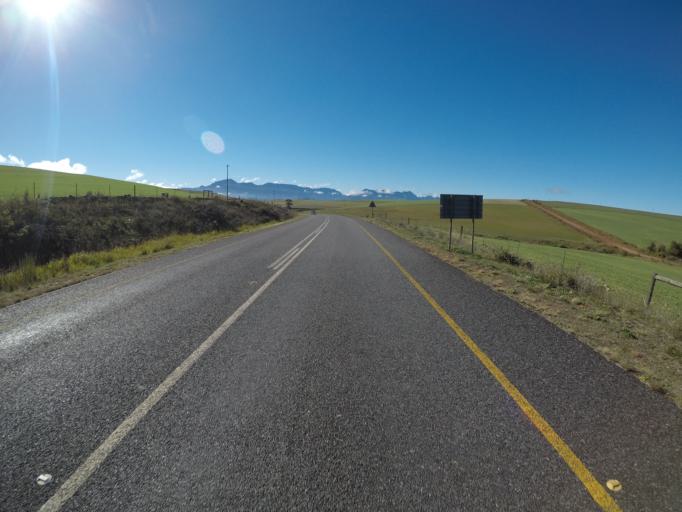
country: ZA
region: Western Cape
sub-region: Overberg District Municipality
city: Caledon
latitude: -34.1383
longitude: 19.5062
